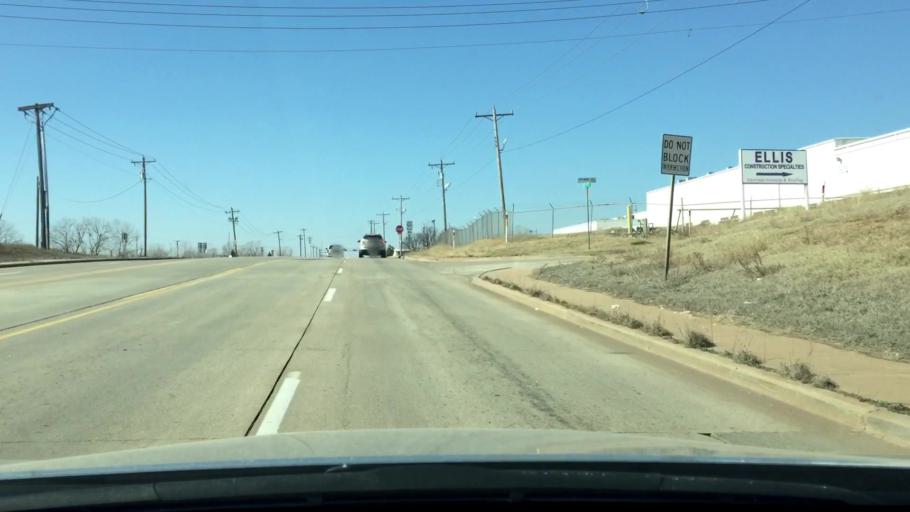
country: US
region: Oklahoma
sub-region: Oklahoma County
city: The Village
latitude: 35.5946
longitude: -97.5087
